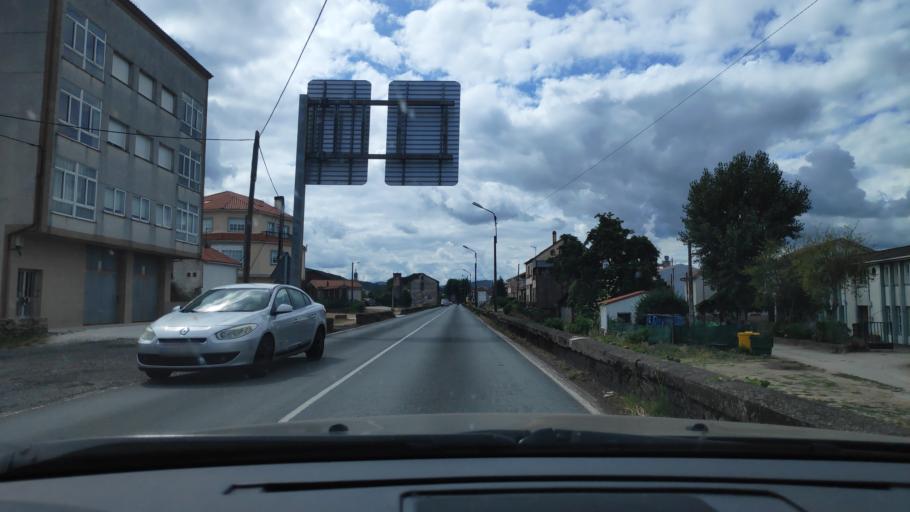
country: ES
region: Galicia
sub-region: Provincia da Coruna
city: Padron
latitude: 42.7283
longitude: -8.6570
